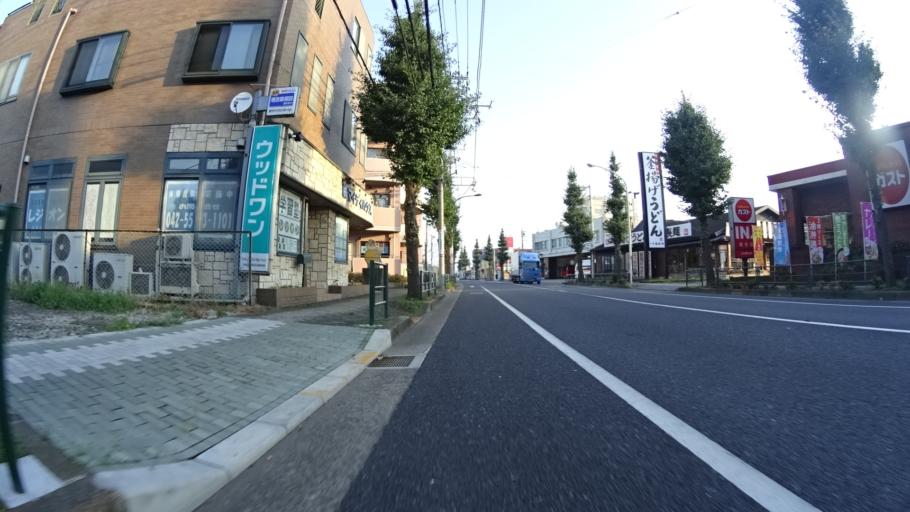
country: JP
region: Tokyo
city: Fussa
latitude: 35.7432
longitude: 139.3246
